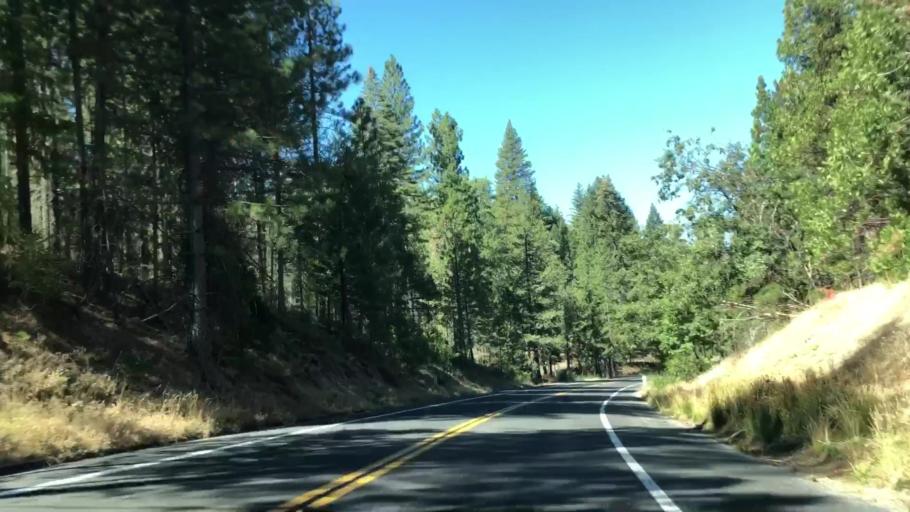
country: US
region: California
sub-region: Mariposa County
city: Midpines
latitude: 37.8133
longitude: -119.8939
